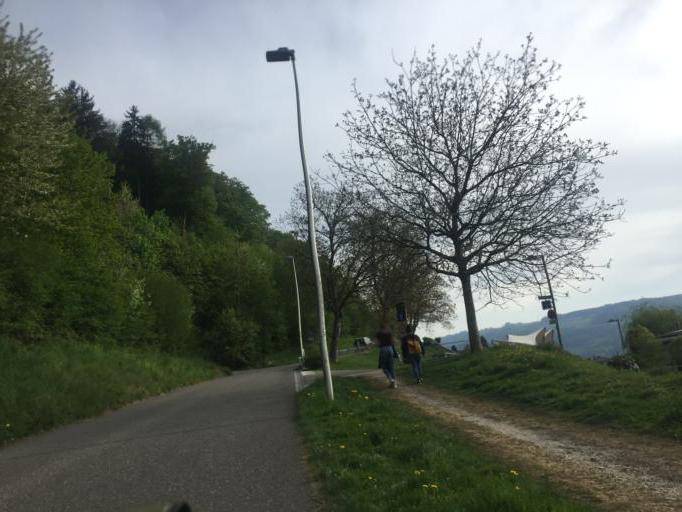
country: CH
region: Bern
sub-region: Bern-Mittelland District
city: Belp
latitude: 46.8810
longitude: 7.5086
